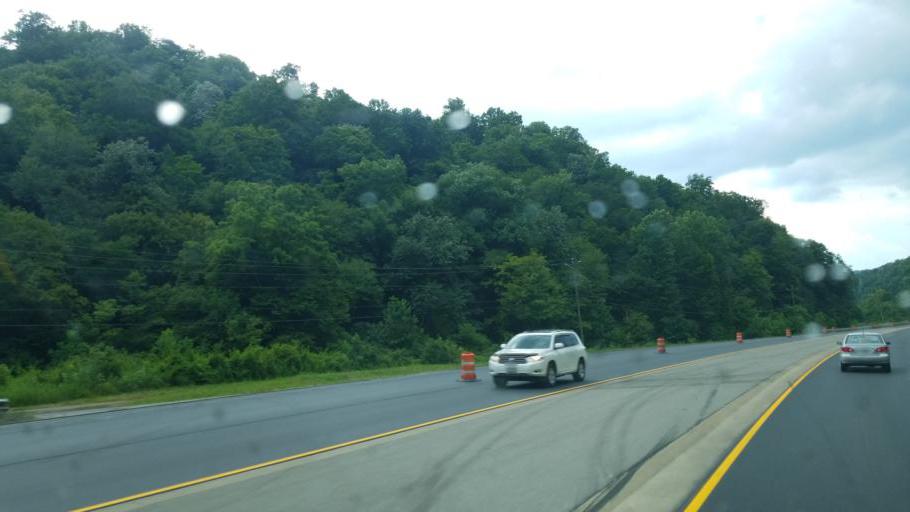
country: US
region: Kentucky
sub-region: Pike County
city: Pikeville
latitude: 37.5083
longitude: -82.5142
